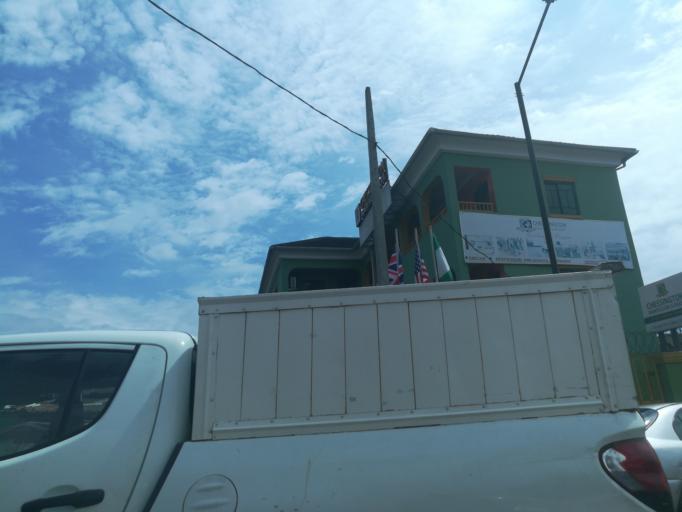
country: NG
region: Lagos
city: Agege
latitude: 6.6220
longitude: 3.3275
